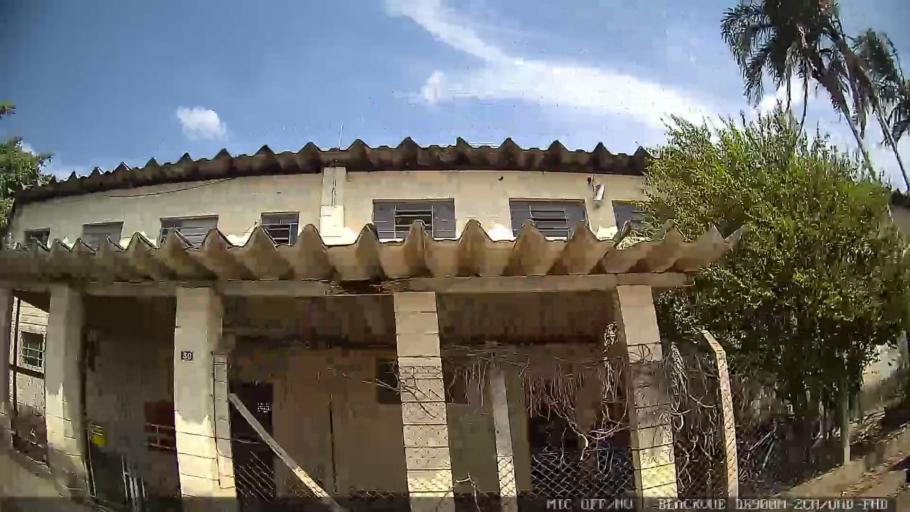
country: BR
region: Sao Paulo
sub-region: Cabreuva
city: Cabreuva
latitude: -23.2485
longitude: -47.0610
